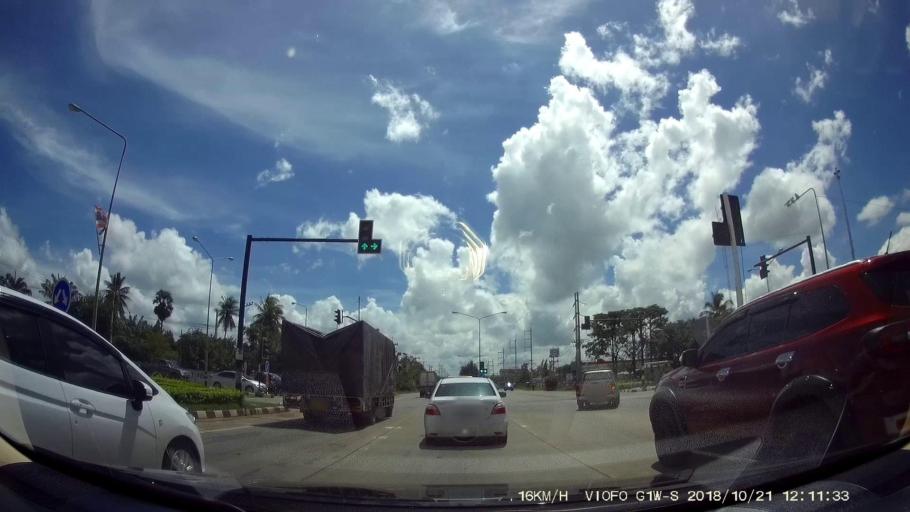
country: TH
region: Chaiyaphum
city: Chatturat
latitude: 15.4144
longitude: 101.8335
